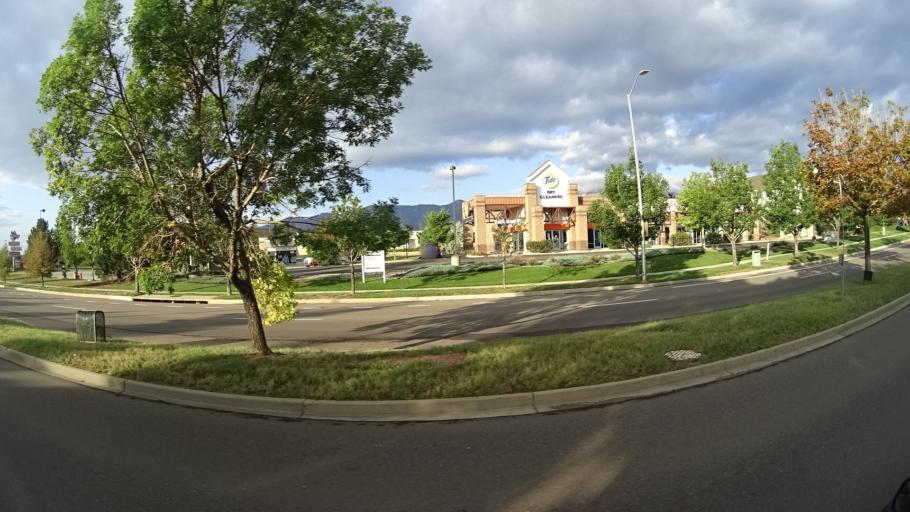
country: US
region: Colorado
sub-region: El Paso County
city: Colorado Springs
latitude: 38.8998
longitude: -104.8516
